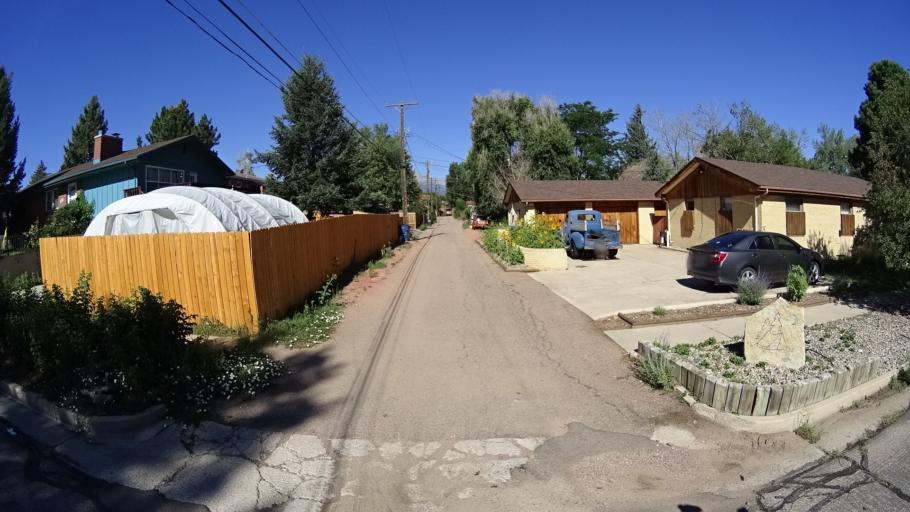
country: US
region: Colorado
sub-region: El Paso County
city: Colorado Springs
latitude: 38.8547
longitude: -104.7827
